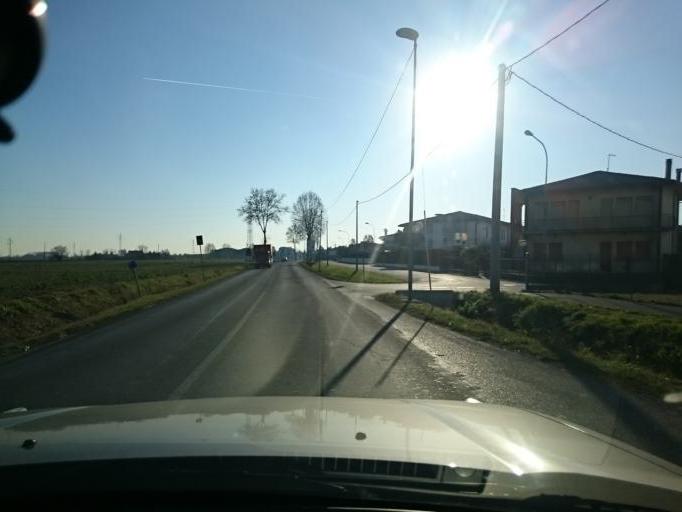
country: IT
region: Veneto
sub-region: Provincia di Venezia
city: Fiesso
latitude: 45.4098
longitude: 12.0521
